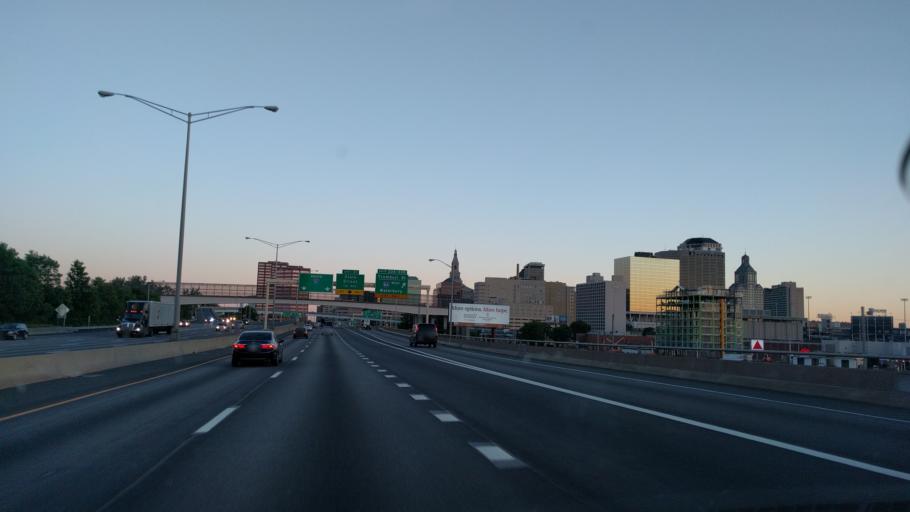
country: US
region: Connecticut
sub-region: Hartford County
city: Hartford
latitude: 41.7752
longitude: -72.6682
